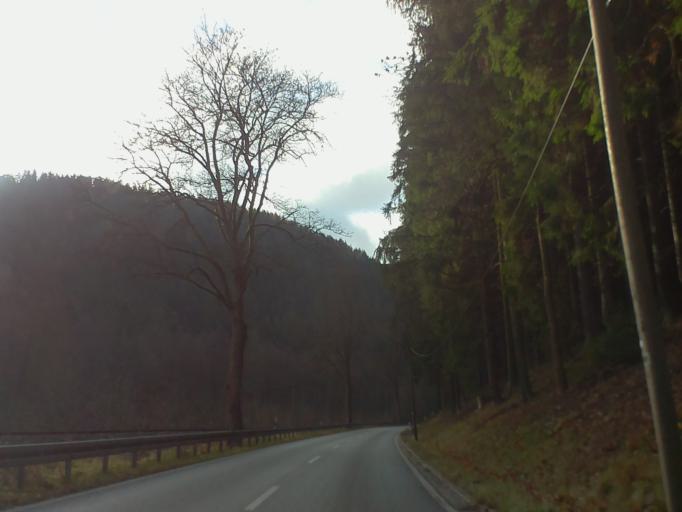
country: DE
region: Thuringia
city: Mellenbach-Glasbach
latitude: 50.6056
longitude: 11.0874
